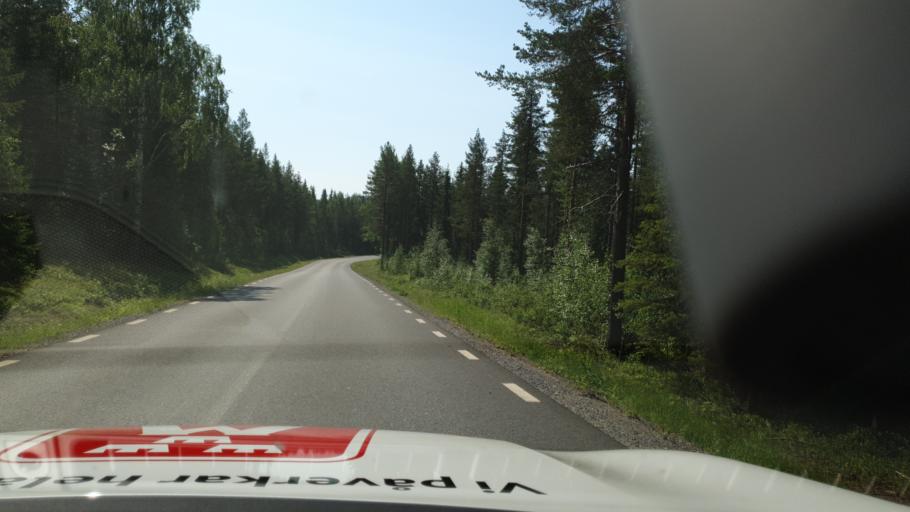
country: SE
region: Vaesterbotten
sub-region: Skelleftea Kommun
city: Langsele
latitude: 64.9651
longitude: 20.0437
